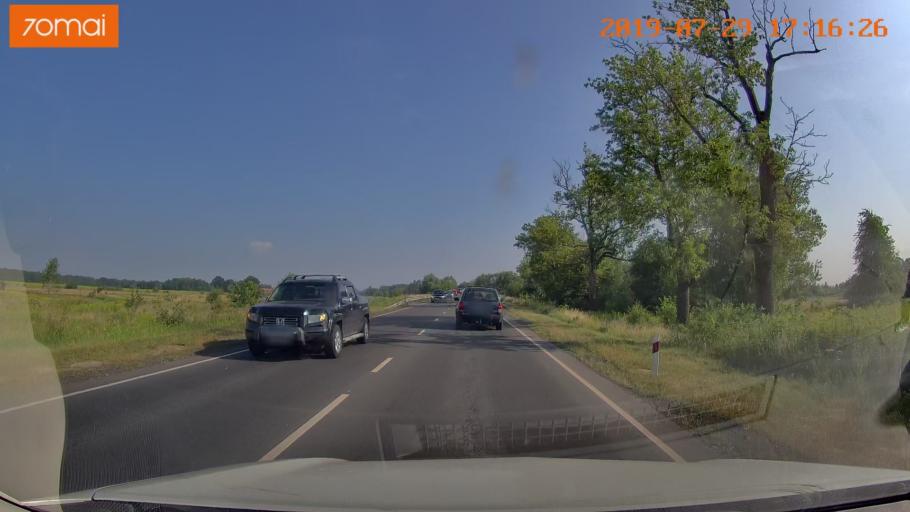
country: RU
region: Kaliningrad
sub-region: Gorod Kaliningrad
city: Kaliningrad
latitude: 54.7801
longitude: 20.4153
